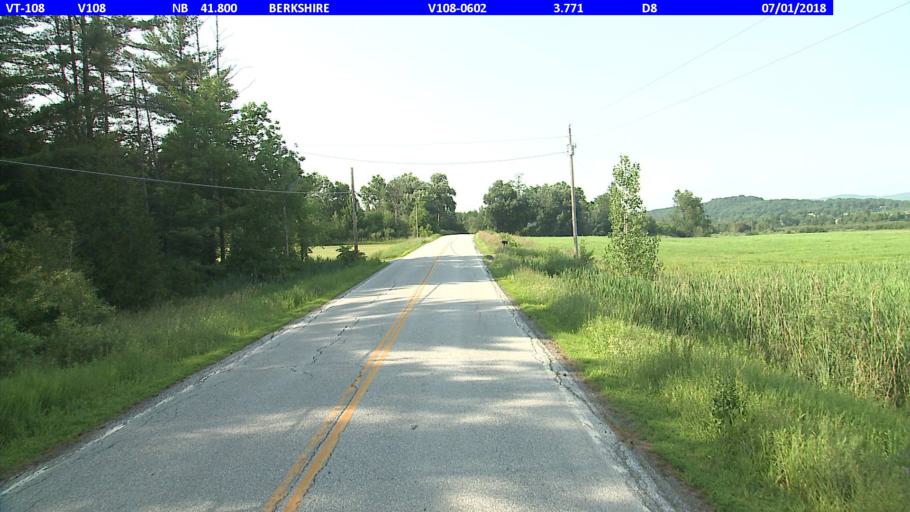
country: US
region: Vermont
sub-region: Franklin County
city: Enosburg Falls
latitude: 44.9766
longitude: -72.8225
